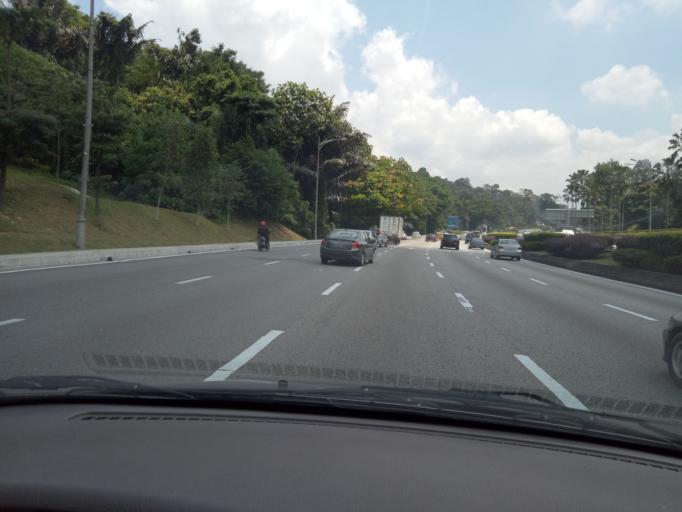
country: MY
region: Kuala Lumpur
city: Kuala Lumpur
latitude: 3.1387
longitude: 101.6831
